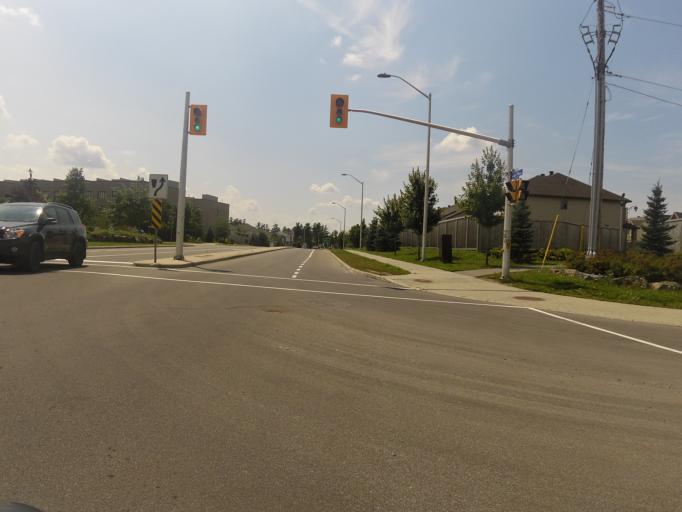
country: CA
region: Ontario
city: Bells Corners
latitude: 45.3221
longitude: -75.9261
